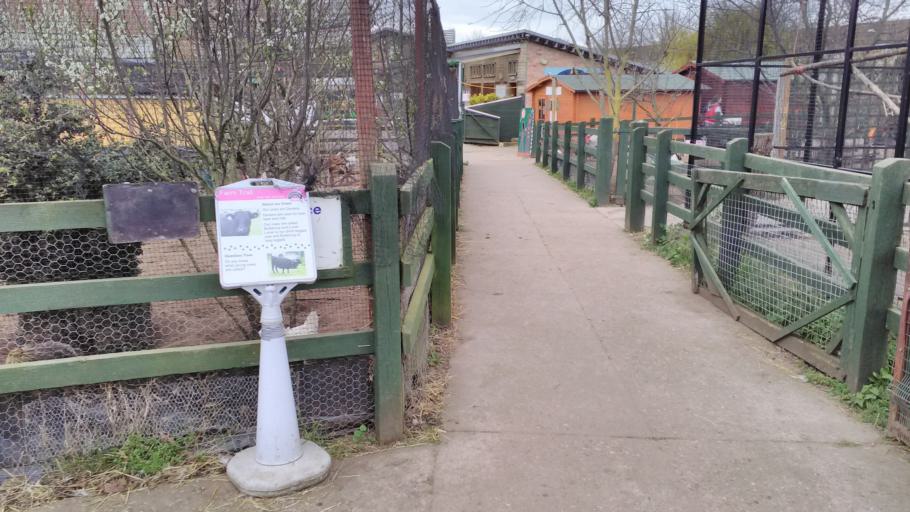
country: GB
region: England
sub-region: Nottingham
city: Nottingham
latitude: 52.9579
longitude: -1.1337
